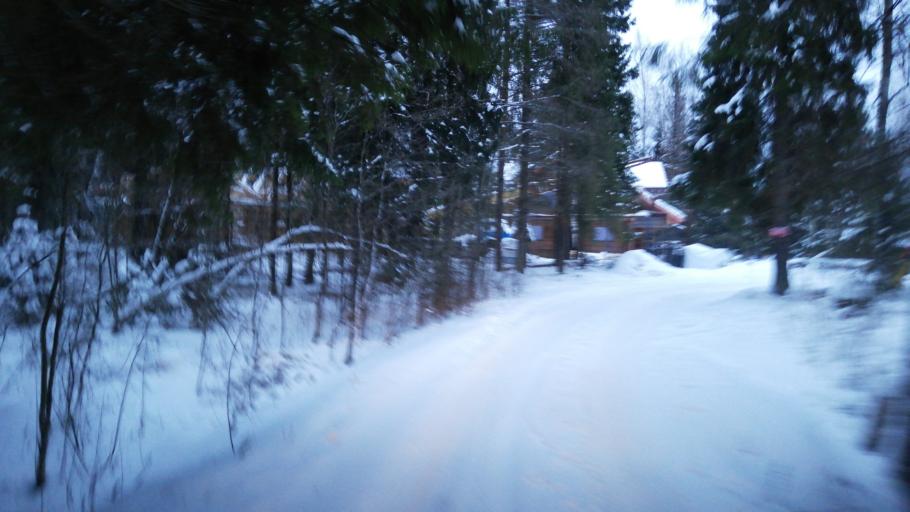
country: RU
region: Jaroslavl
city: Krasnyye Tkachi
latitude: 57.4468
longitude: 39.7993
